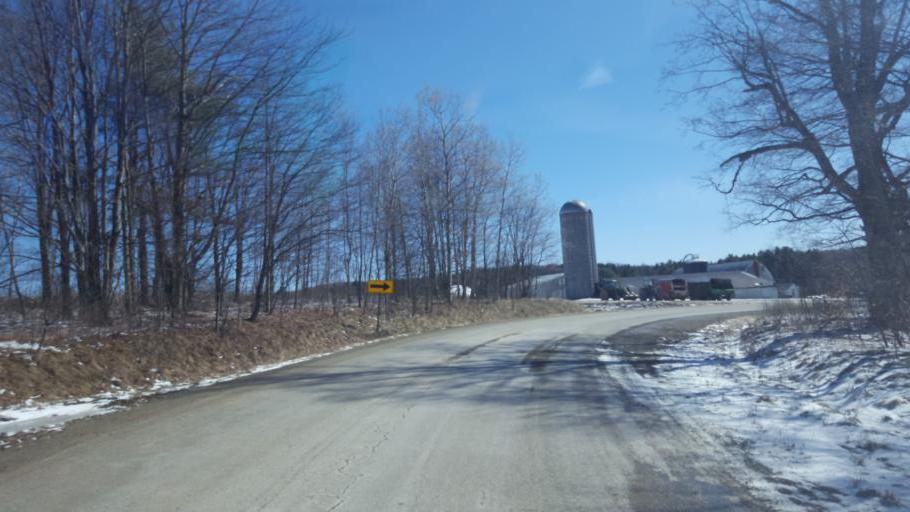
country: US
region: New York
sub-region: Allegany County
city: Andover
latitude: 41.9945
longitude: -77.7632
